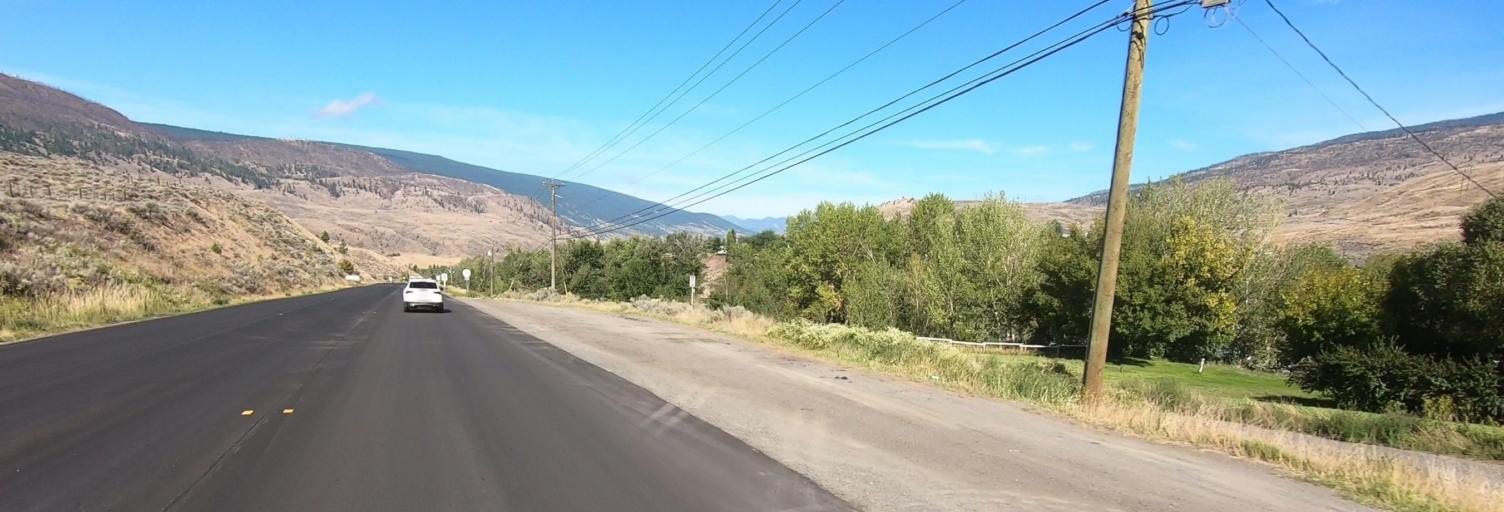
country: CA
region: British Columbia
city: Cache Creek
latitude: 50.8095
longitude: -121.3072
